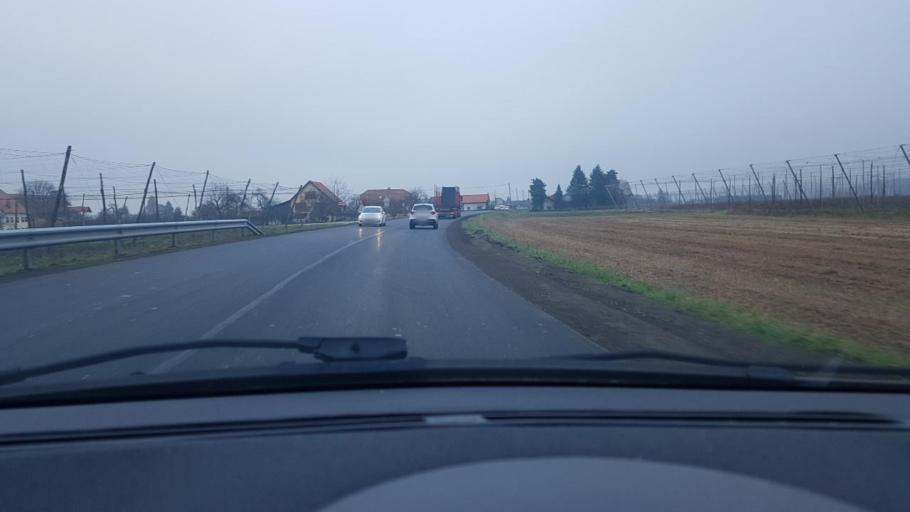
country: SI
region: Tabor
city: Tabor
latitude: 46.2484
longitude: 15.0205
